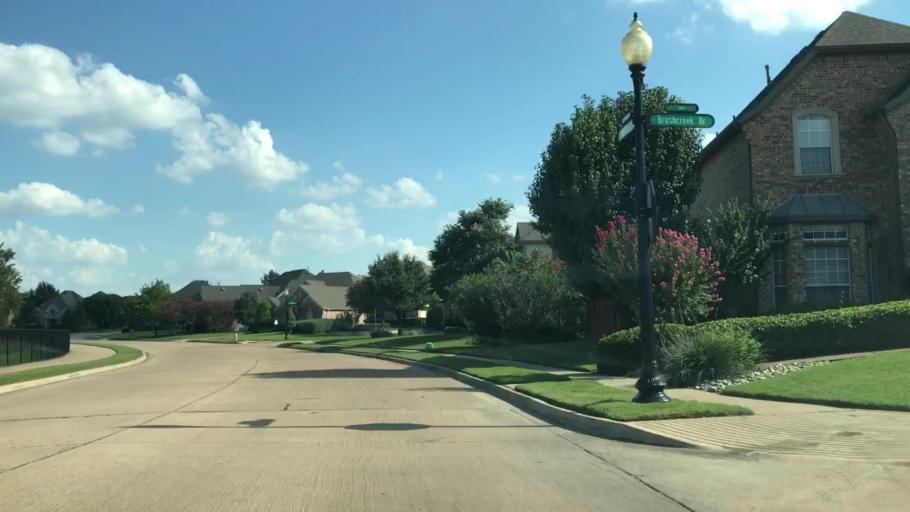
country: US
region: Texas
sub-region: Tarrant County
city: Keller
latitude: 32.9202
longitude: -97.1972
